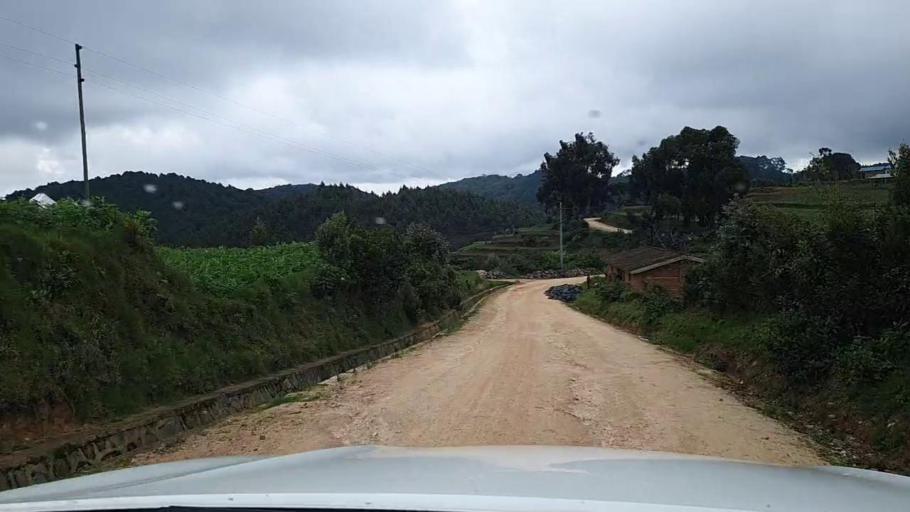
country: RW
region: Southern Province
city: Nzega
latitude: -2.3769
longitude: 29.3824
